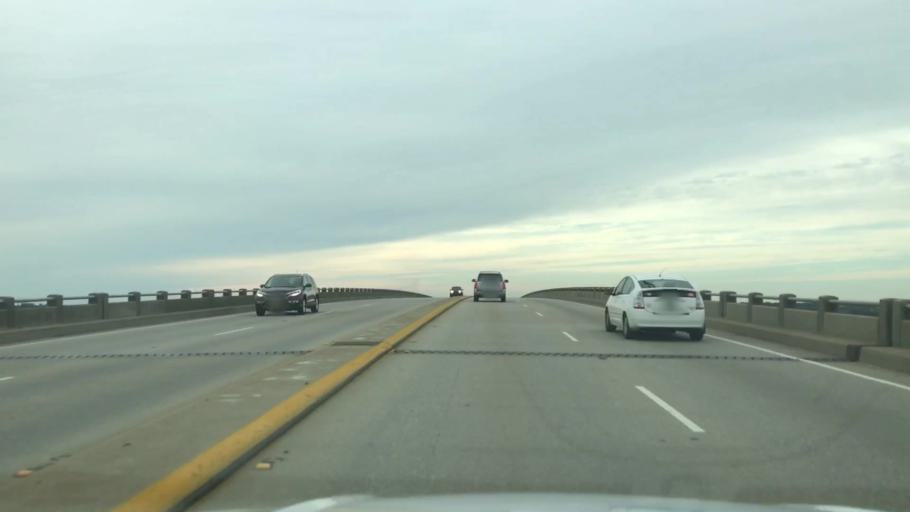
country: US
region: South Carolina
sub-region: Georgetown County
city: Georgetown
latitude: 33.3659
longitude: -79.2522
